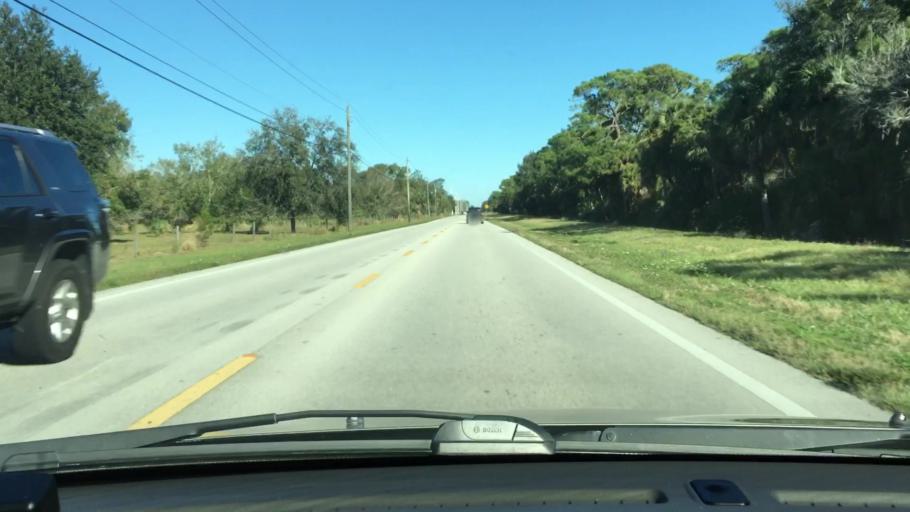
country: US
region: Florida
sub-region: Indian River County
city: Winter Beach
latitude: 27.7135
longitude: -80.4625
